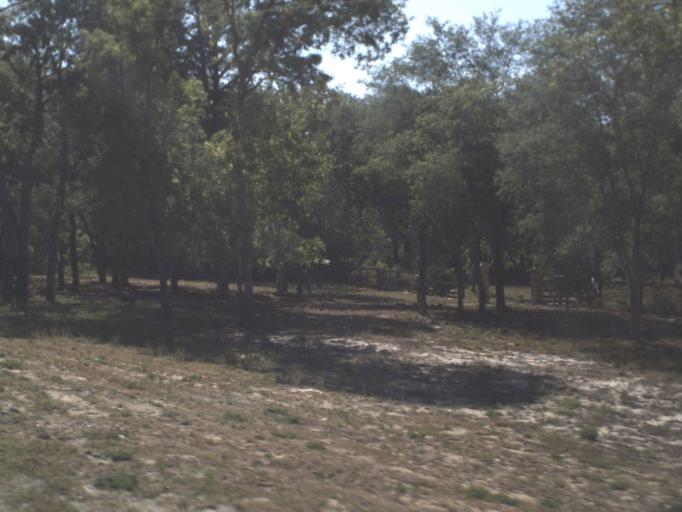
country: US
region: Florida
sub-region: Marion County
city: Dunnellon
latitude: 29.1321
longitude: -82.4034
